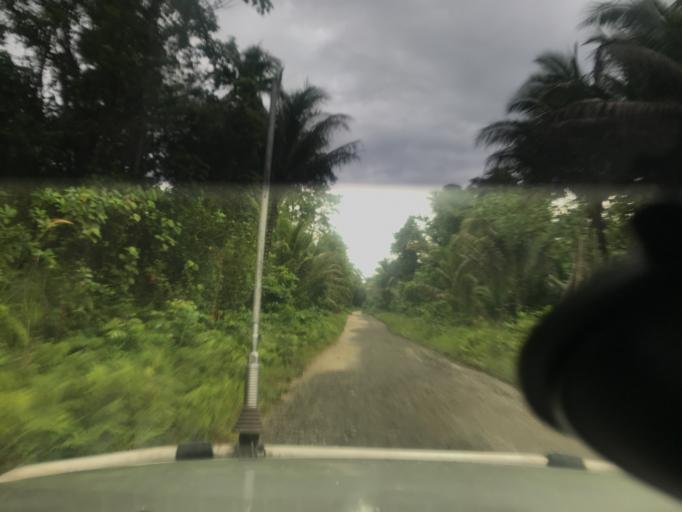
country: SB
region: Malaita
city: Auki
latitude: -8.9138
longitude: 160.7688
